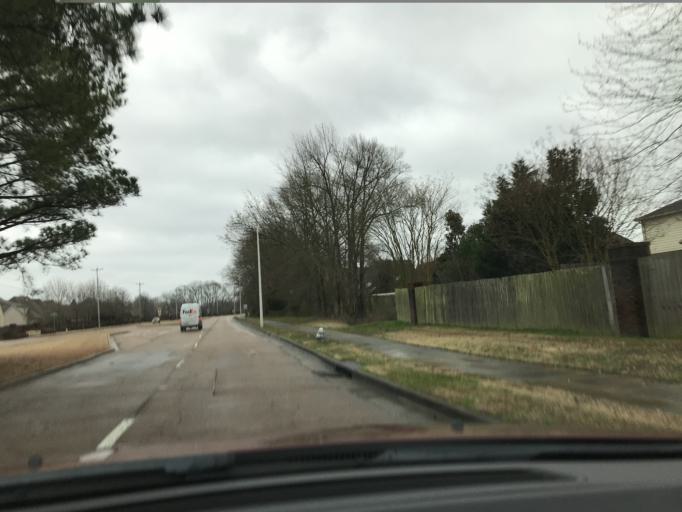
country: US
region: Tennessee
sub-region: Shelby County
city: Collierville
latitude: 35.0851
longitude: -89.6880
